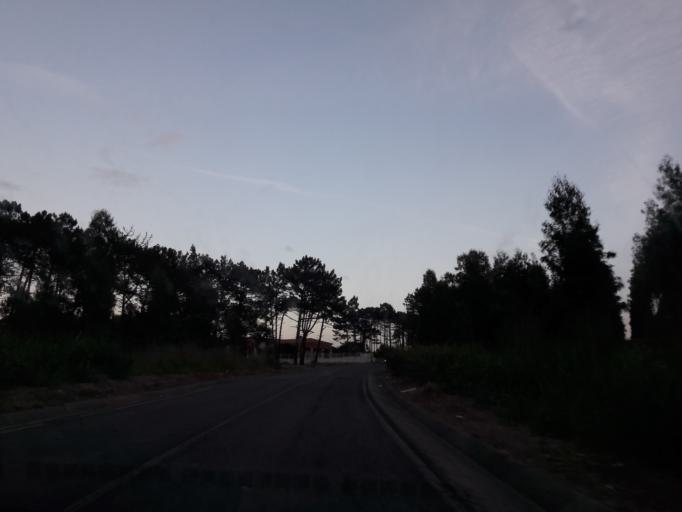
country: PT
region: Leiria
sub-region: Peniche
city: Atouguia da Baleia
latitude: 39.3563
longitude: -9.2952
